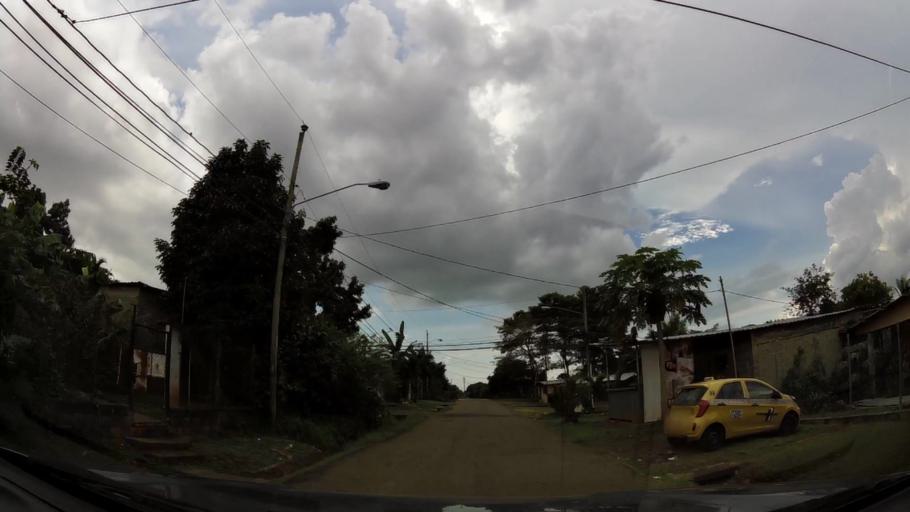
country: PA
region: Panama
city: Cabra Numero Uno
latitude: 9.1074
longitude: -79.3210
